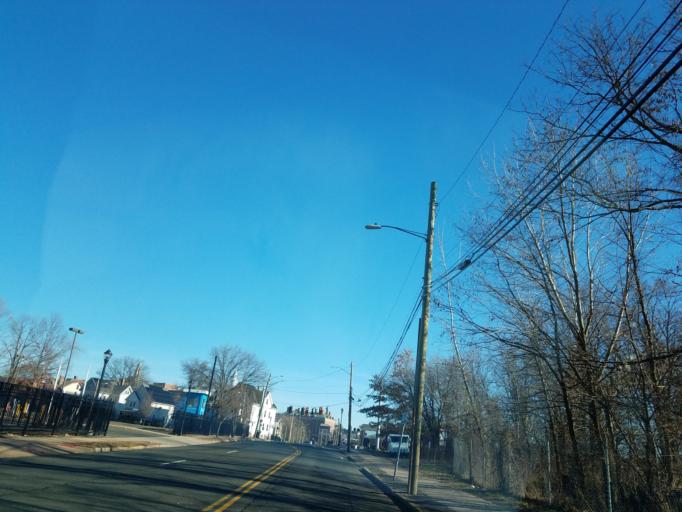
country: US
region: Connecticut
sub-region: Hartford County
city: Hartford
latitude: 41.7635
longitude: -72.6982
